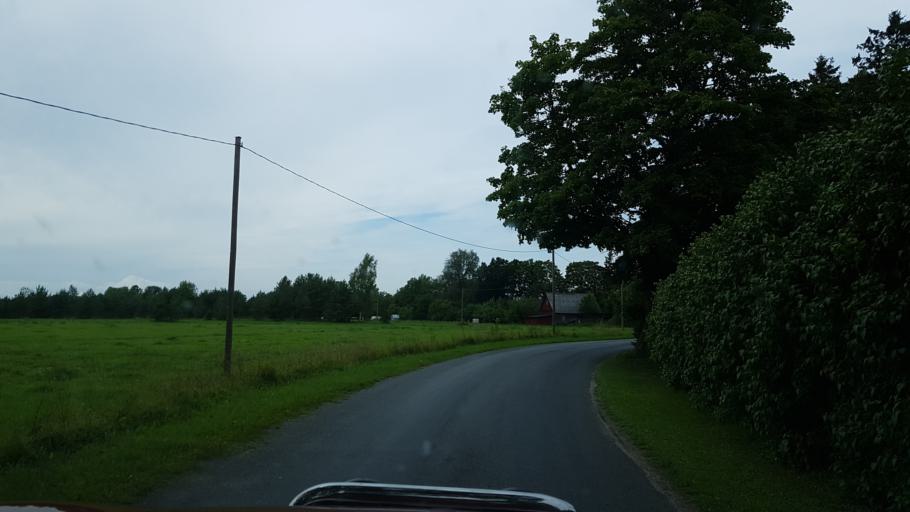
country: EE
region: Laeaene
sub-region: Ridala Parish
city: Uuemoisa
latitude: 59.0127
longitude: 23.7231
